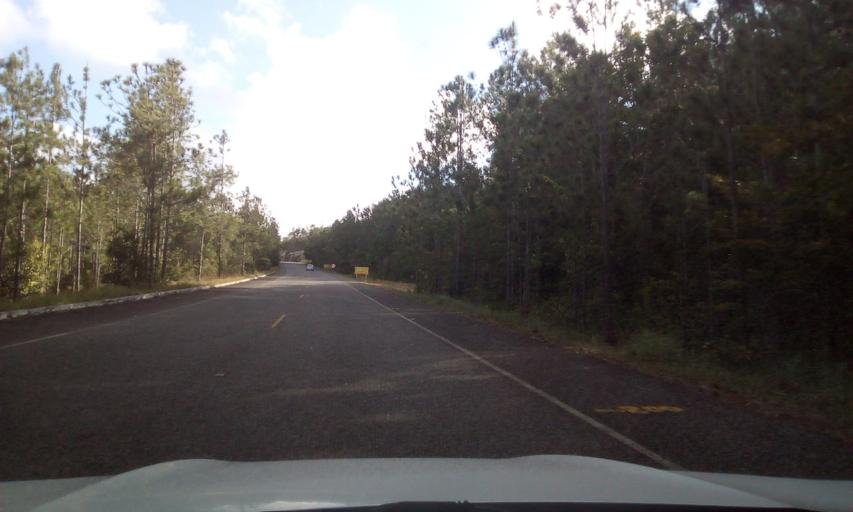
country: BR
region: Bahia
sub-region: Conde
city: Conde
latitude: -12.0987
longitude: -37.7764
